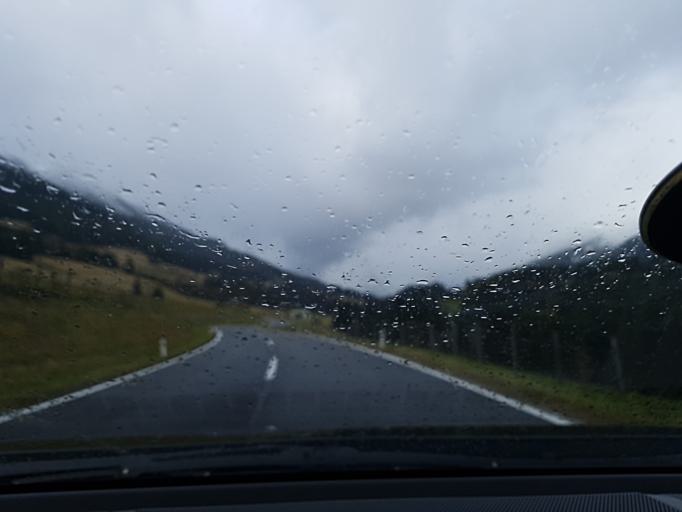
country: AT
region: Styria
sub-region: Politischer Bezirk Murtal
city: Sankt Johann am Tauern
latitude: 47.3676
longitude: 14.4629
